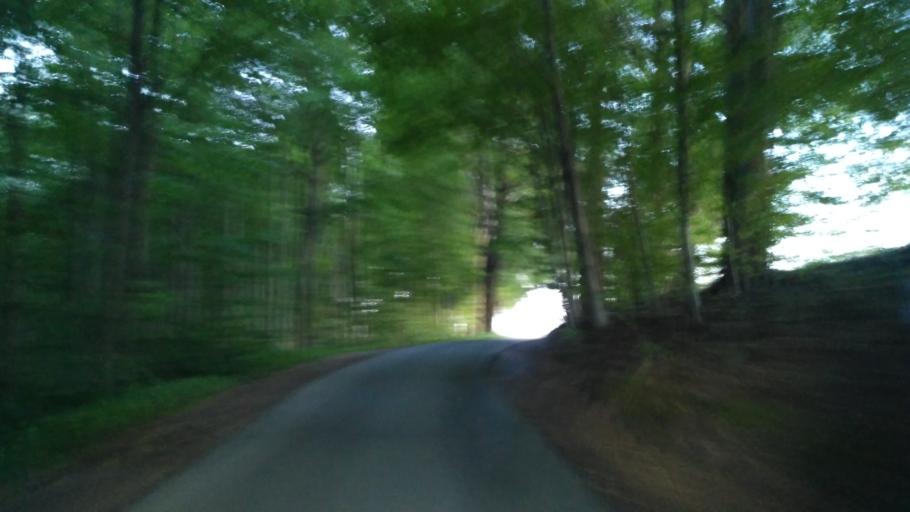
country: PL
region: Subcarpathian Voivodeship
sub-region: Powiat strzyzowski
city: Czudec
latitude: 49.9213
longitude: 21.8369
